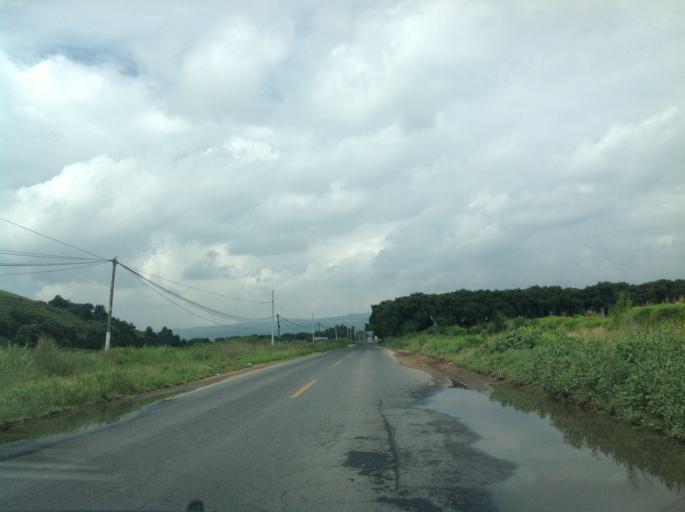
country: MX
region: Mexico
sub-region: Rayon
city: Colonia Emiliano Zapata
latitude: 19.1152
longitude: -99.5619
